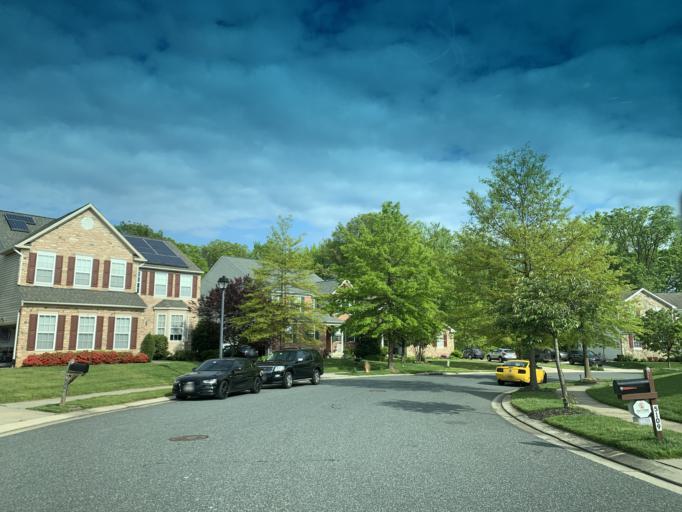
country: US
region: Maryland
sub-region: Baltimore County
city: White Marsh
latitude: 39.4032
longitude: -76.4269
